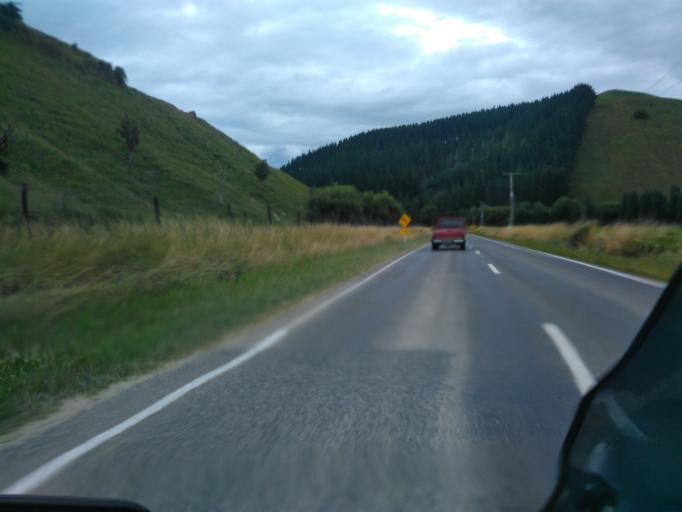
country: NZ
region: Gisborne
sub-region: Gisborne District
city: Gisborne
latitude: -38.4613
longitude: 177.7428
